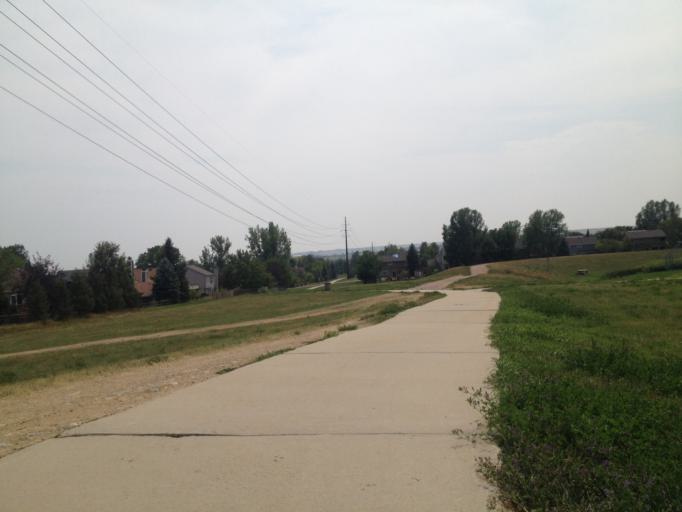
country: US
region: Colorado
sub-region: Boulder County
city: Superior
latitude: 39.9742
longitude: -105.1565
